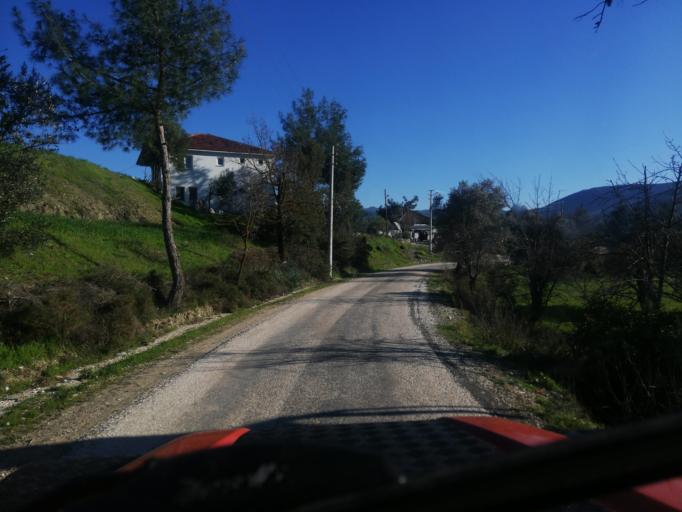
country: TR
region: Antalya
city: Kas
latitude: 36.2920
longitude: 29.7064
